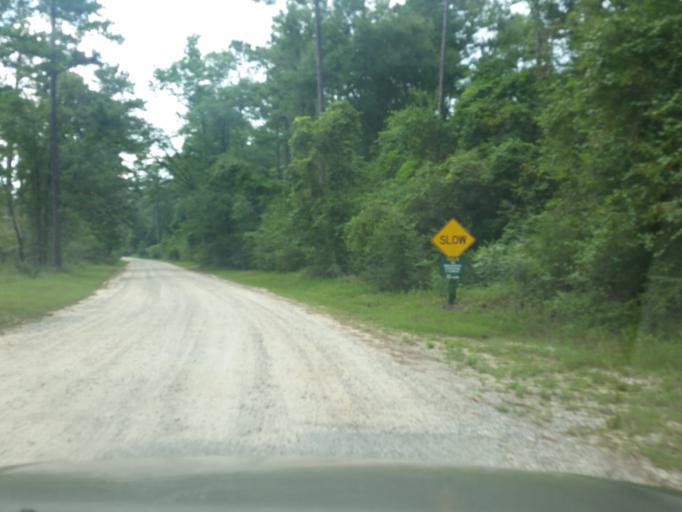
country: US
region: Alabama
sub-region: Baldwin County
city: Spanish Fort
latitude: 30.7414
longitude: -87.9099
